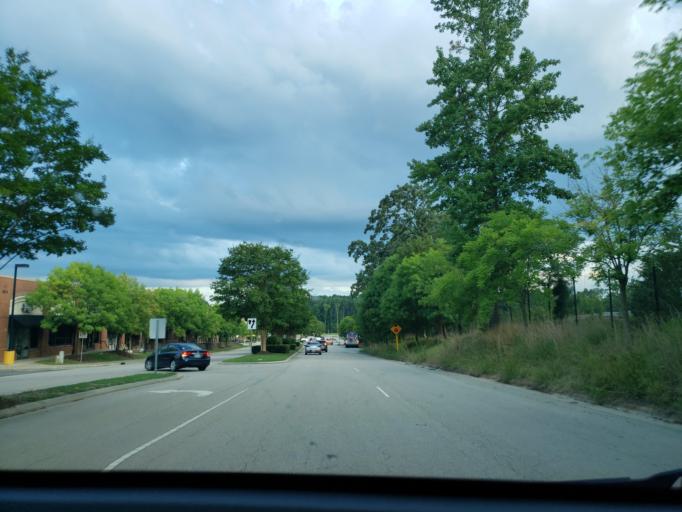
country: US
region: North Carolina
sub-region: Orange County
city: Chapel Hill
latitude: 35.9521
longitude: -78.9897
